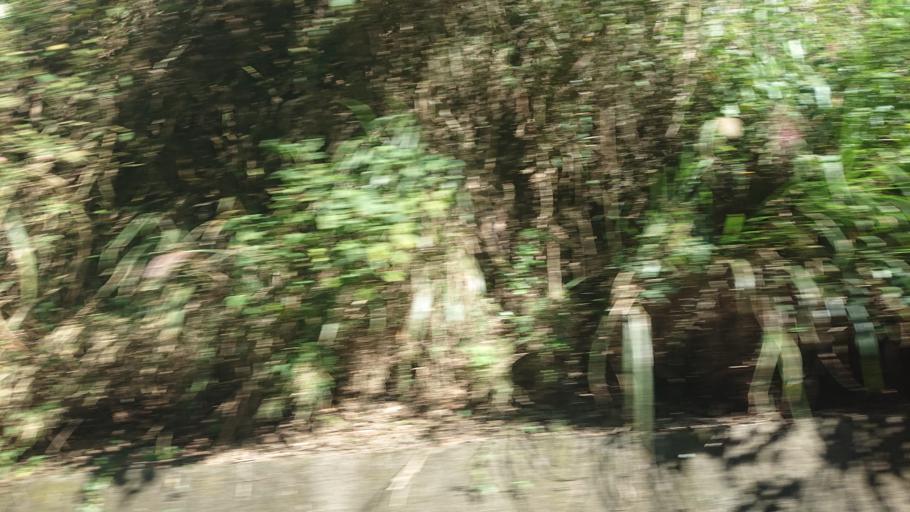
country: TW
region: Taiwan
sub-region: Chiayi
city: Jiayi Shi
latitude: 23.5266
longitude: 120.6306
